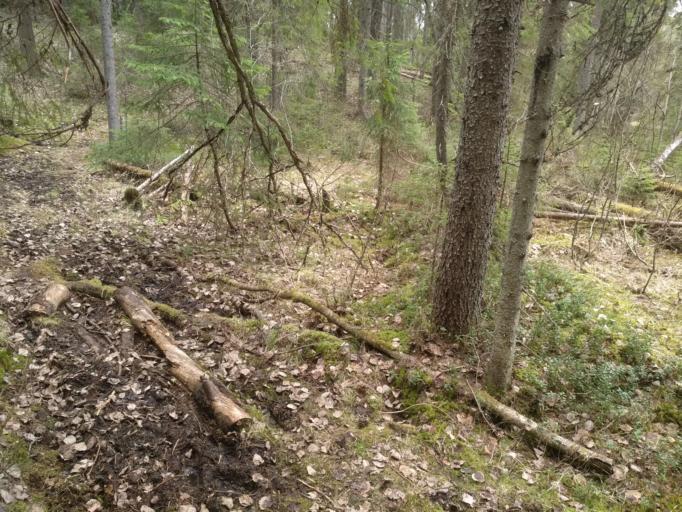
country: RU
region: Leningrad
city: Sosnovo
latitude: 60.4802
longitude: 30.1570
